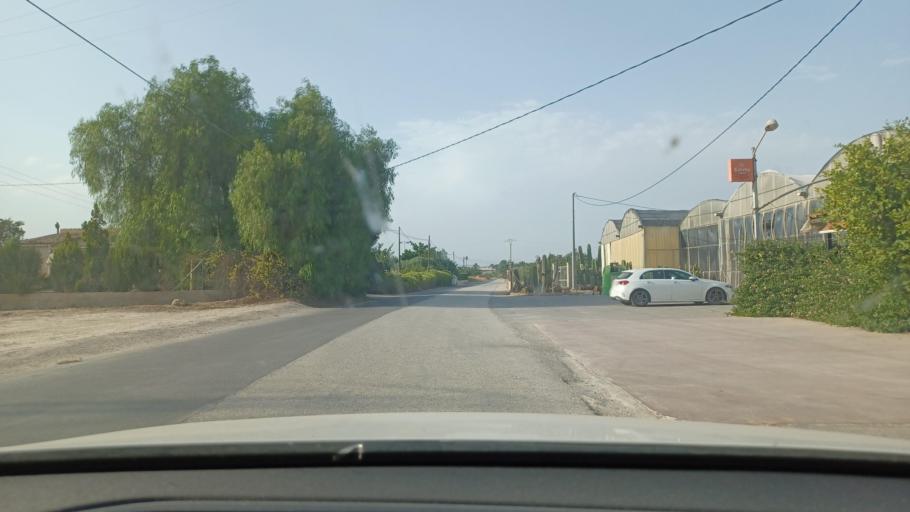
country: ES
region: Valencia
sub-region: Provincia de Alicante
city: Elche
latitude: 38.2435
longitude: -0.6915
